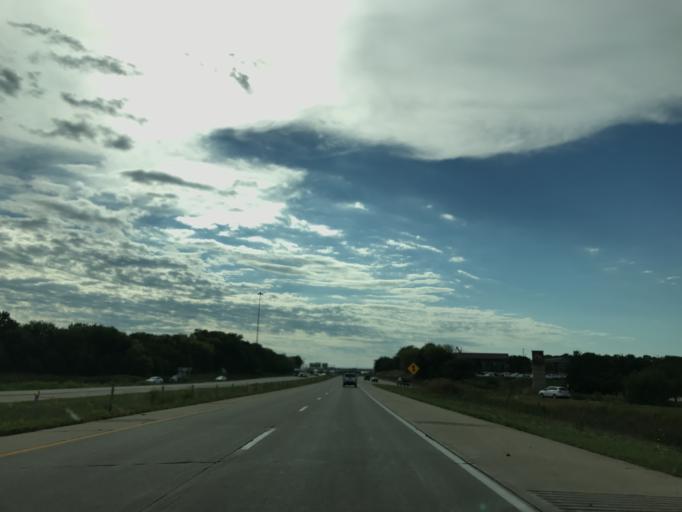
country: US
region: Iowa
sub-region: Polk County
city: Clive
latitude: 41.5924
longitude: -93.7821
